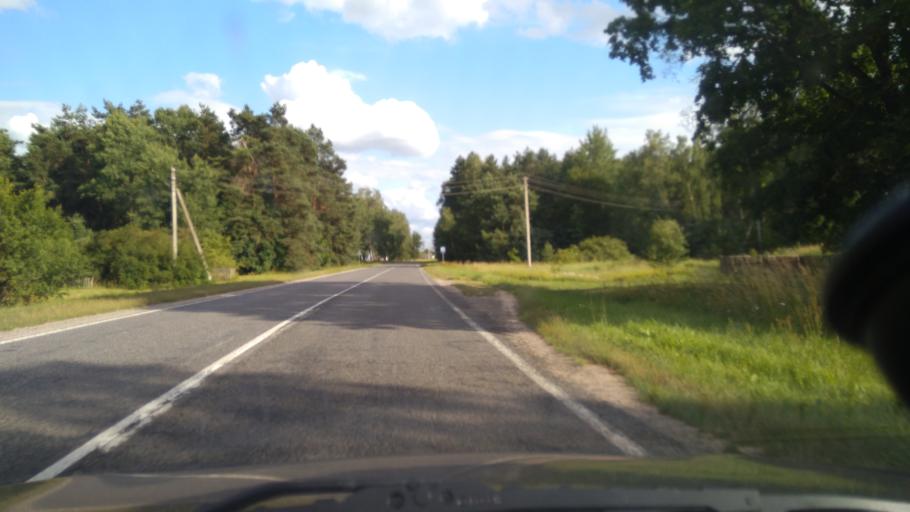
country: BY
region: Grodnenskaya
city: Masty
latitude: 53.3444
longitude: 24.6675
